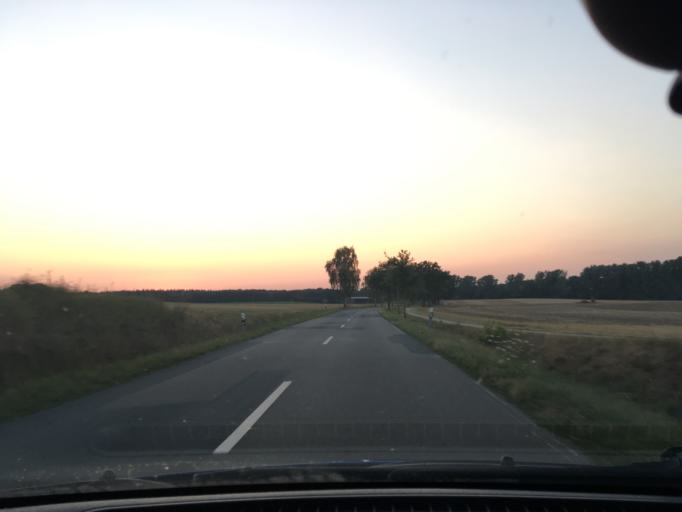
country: DE
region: Lower Saxony
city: Barnstedt
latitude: 53.1512
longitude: 10.3538
